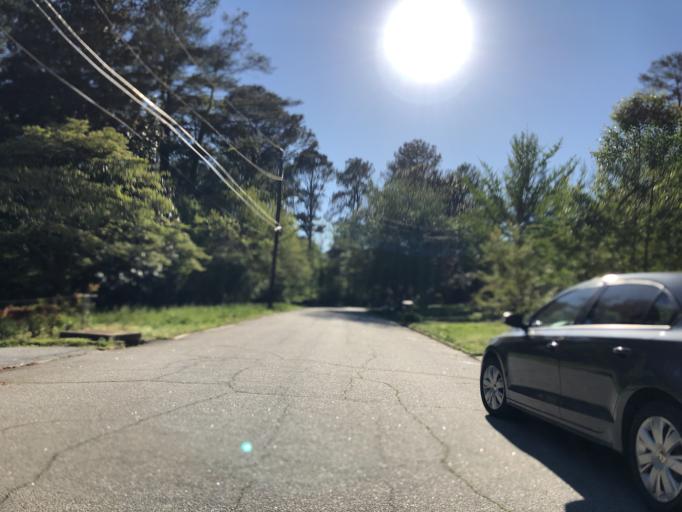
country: US
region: Georgia
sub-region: DeKalb County
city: North Decatur
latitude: 33.8057
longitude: -84.2940
